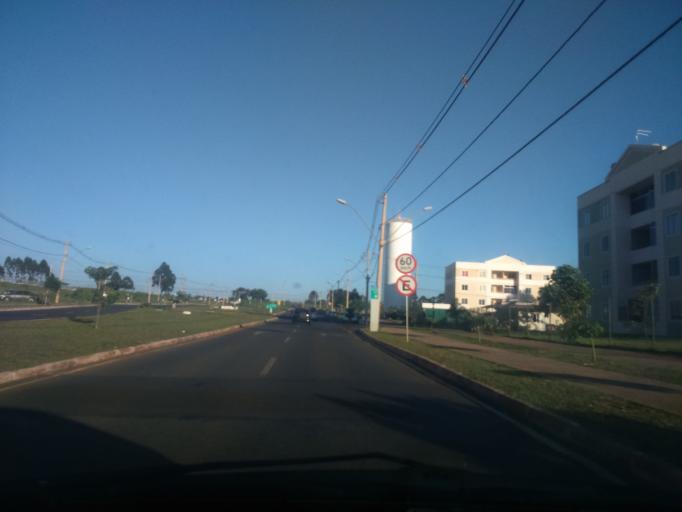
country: BR
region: Federal District
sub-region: Brasilia
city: Brasilia
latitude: -15.8888
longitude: -47.8163
